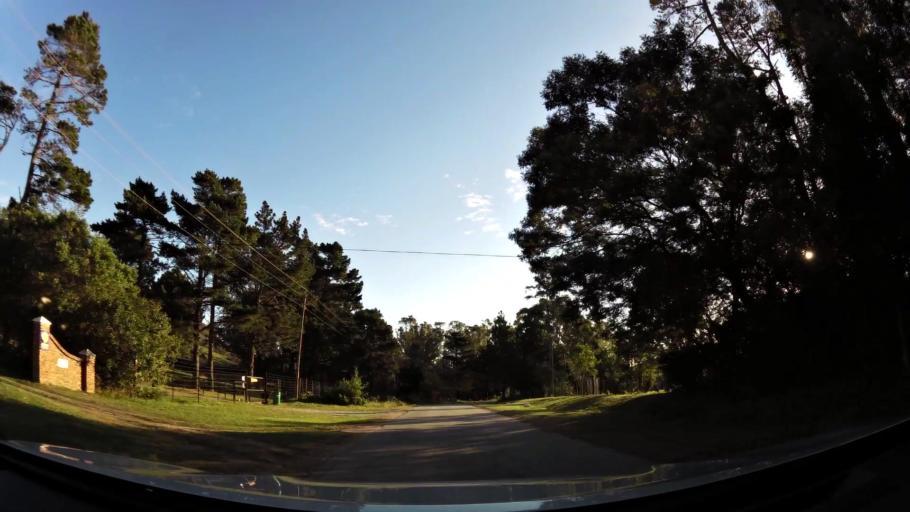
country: ZA
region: Eastern Cape
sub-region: Nelson Mandela Bay Metropolitan Municipality
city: Port Elizabeth
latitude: -33.9884
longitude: 25.4854
